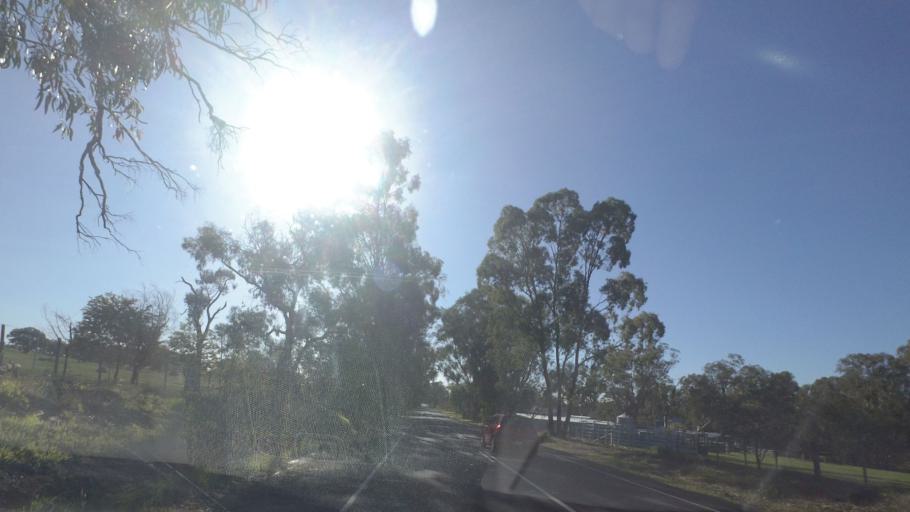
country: AU
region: Victoria
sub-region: Greater Bendigo
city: Kennington
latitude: -36.8906
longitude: 144.3126
